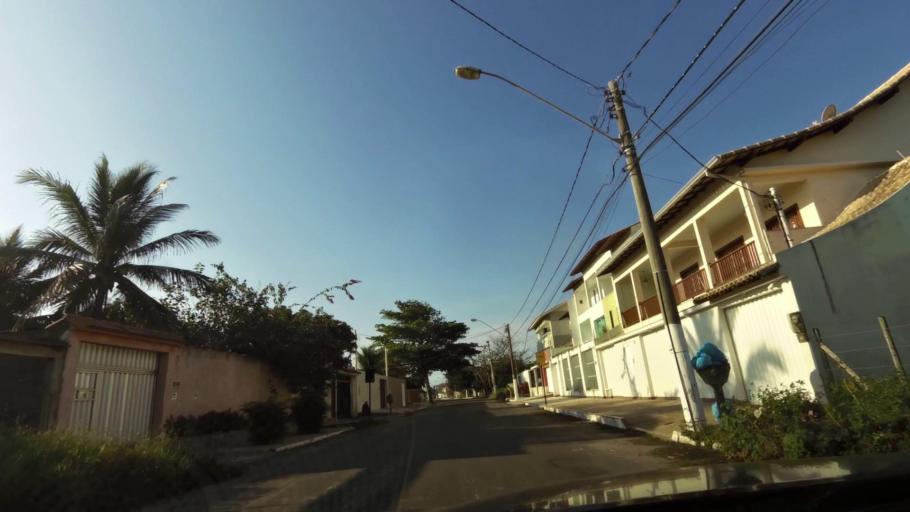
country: BR
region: Espirito Santo
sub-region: Vila Velha
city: Vila Velha
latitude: -20.4832
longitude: -40.3492
